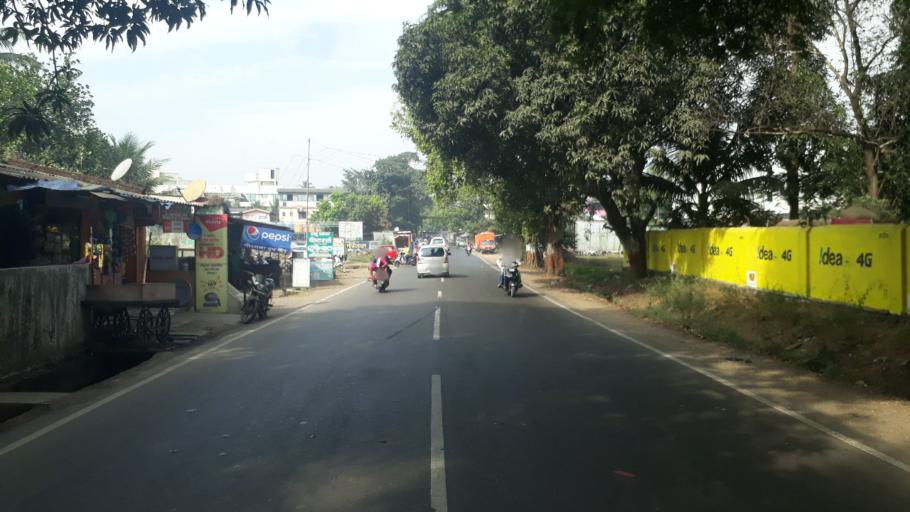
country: IN
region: Maharashtra
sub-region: Raigarh
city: Pen
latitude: 18.6877
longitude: 72.9899
